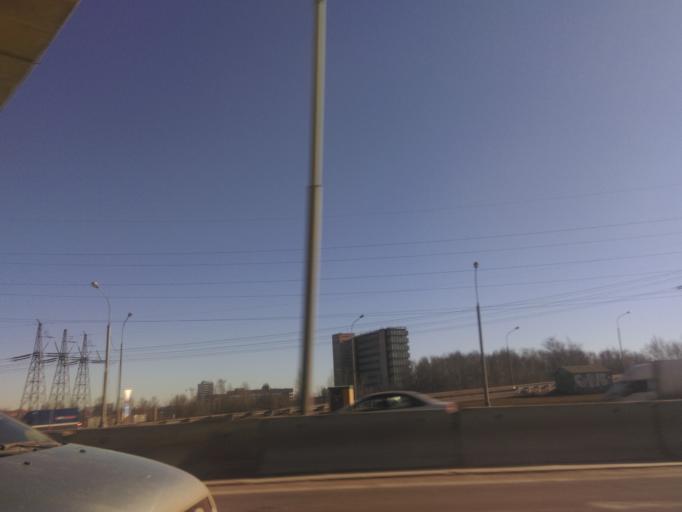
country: RU
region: Moskovskaya
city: Vostryakovo
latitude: 55.6636
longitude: 37.4310
